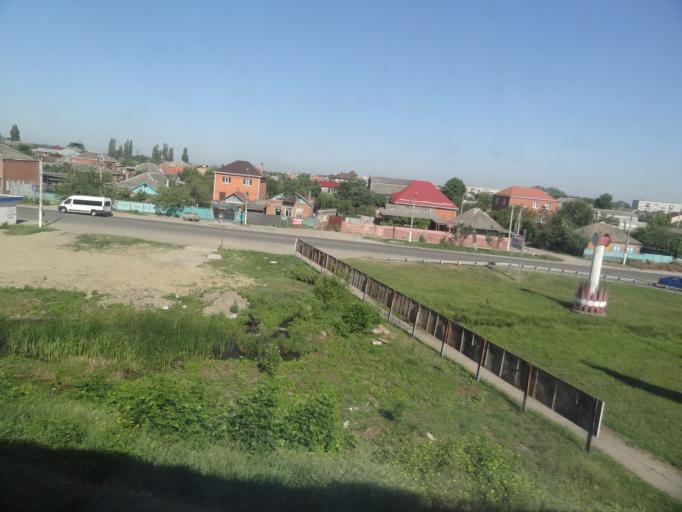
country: RU
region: Adygeya
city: Yablonovskiy
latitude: 44.9827
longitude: 38.9493
